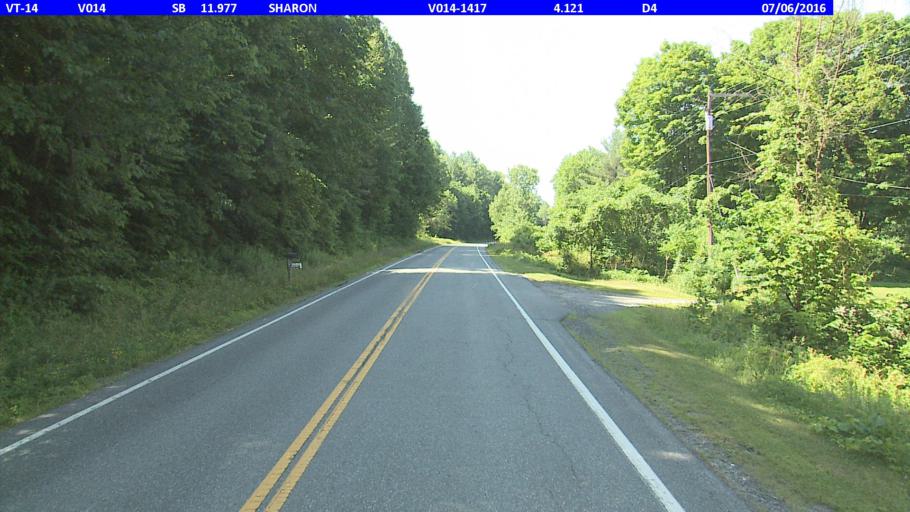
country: US
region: Vermont
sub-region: Windsor County
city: Woodstock
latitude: 43.7750
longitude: -72.4456
